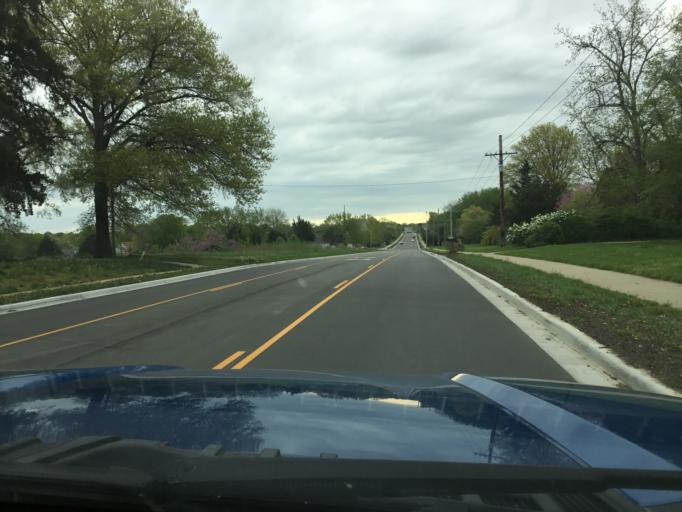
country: US
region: Kansas
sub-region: Douglas County
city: Lawrence
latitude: 38.9861
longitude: -95.2698
